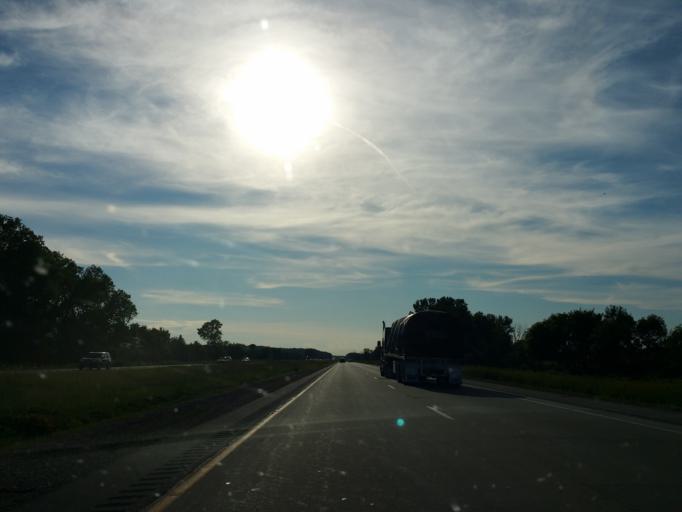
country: US
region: Wisconsin
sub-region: Columbia County
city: Portage
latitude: 43.5244
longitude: -89.5445
